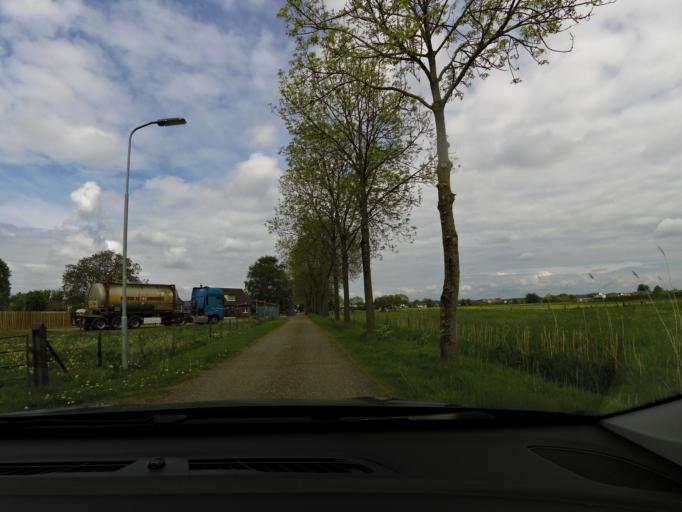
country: NL
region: Gelderland
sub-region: Gemeente Buren
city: Lienden
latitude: 51.9670
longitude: 5.4831
